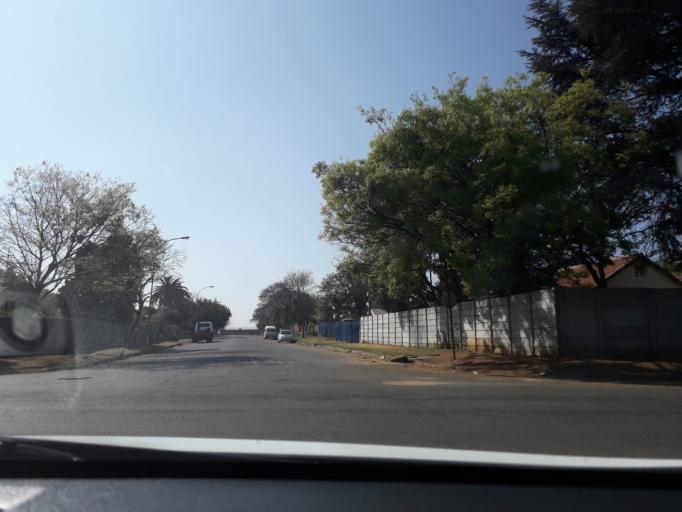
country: ZA
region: Gauteng
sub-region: City of Johannesburg Metropolitan Municipality
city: Modderfontein
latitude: -26.1015
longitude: 28.2423
